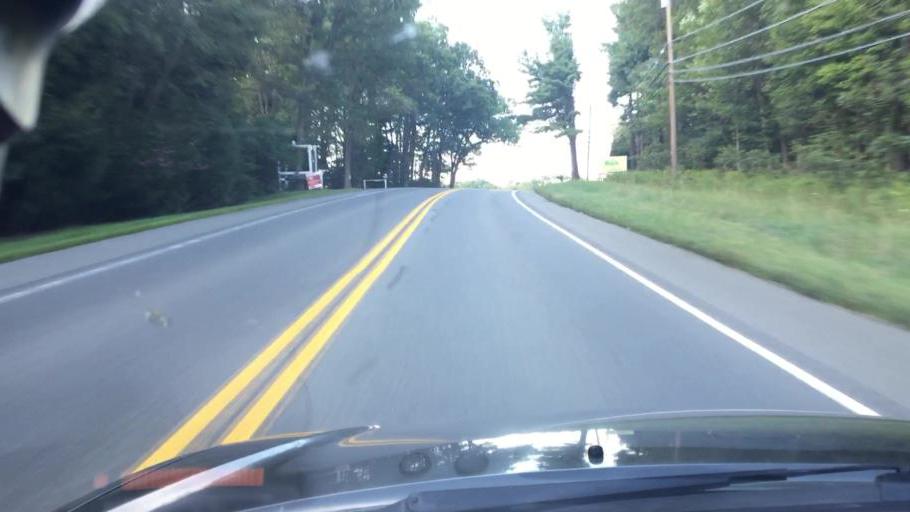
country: US
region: Pennsylvania
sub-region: Carbon County
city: Jim Thorpe
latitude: 40.9032
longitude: -75.6829
